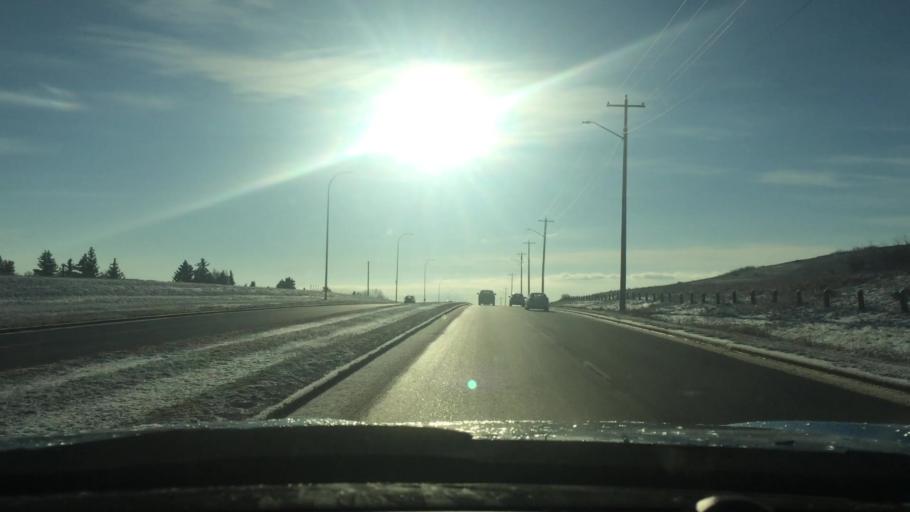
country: CA
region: Alberta
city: Calgary
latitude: 51.1213
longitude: -114.0919
